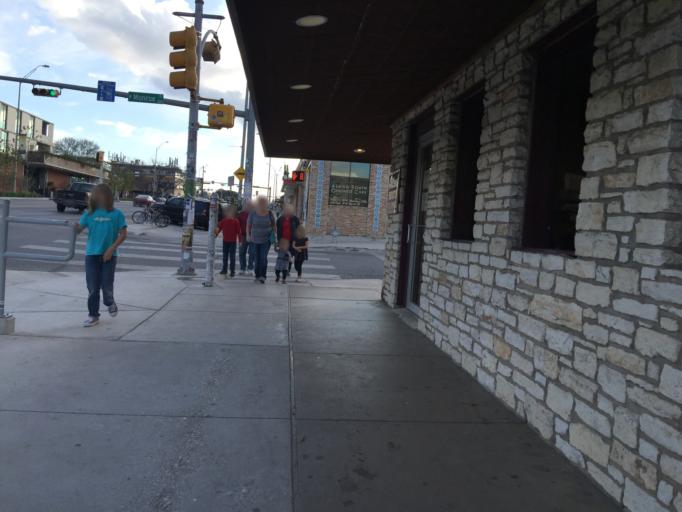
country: US
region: Texas
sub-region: Travis County
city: Austin
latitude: 30.2482
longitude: -97.7504
